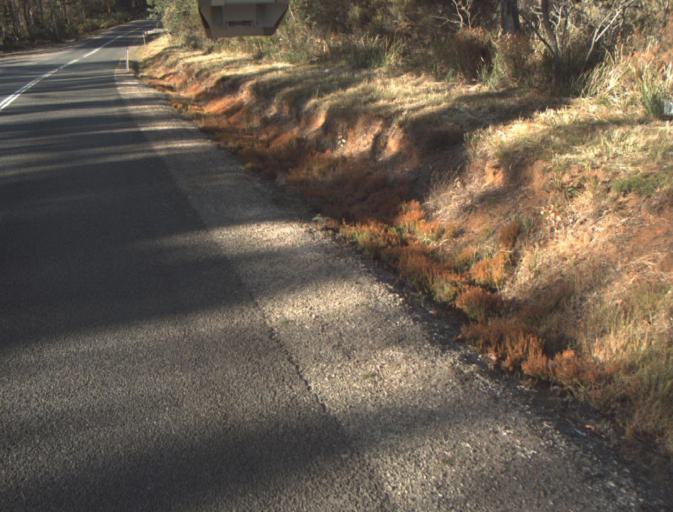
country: AU
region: Tasmania
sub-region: Launceston
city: Mayfield
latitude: -41.3334
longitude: 147.1790
